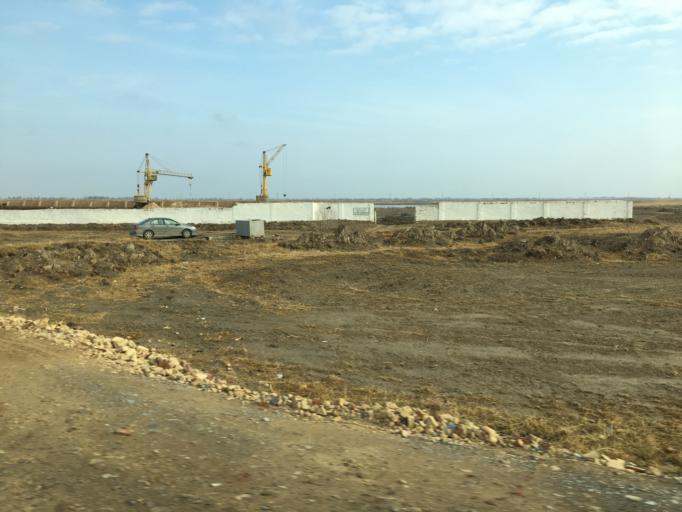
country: TM
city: Murgab
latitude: 37.4783
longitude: 62.0102
